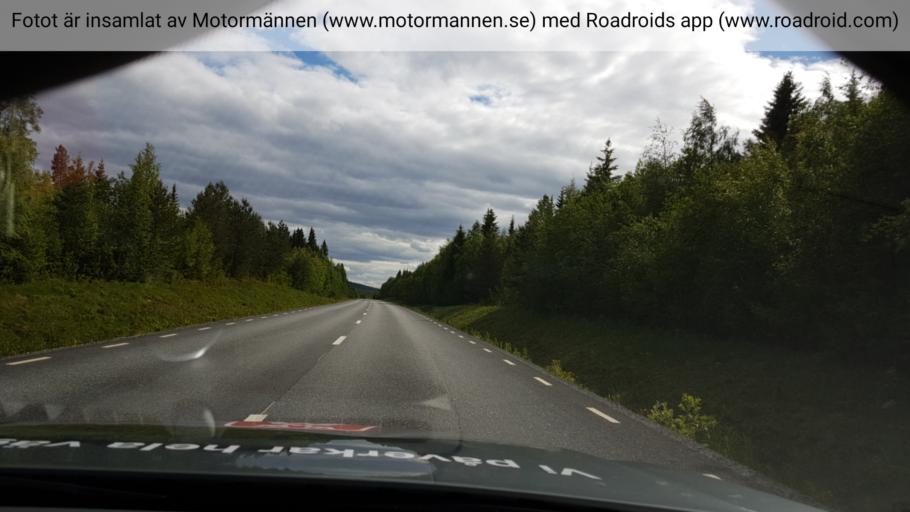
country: SE
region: Jaemtland
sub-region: Stroemsunds Kommun
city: Stroemsund
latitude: 64.0474
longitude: 15.5422
